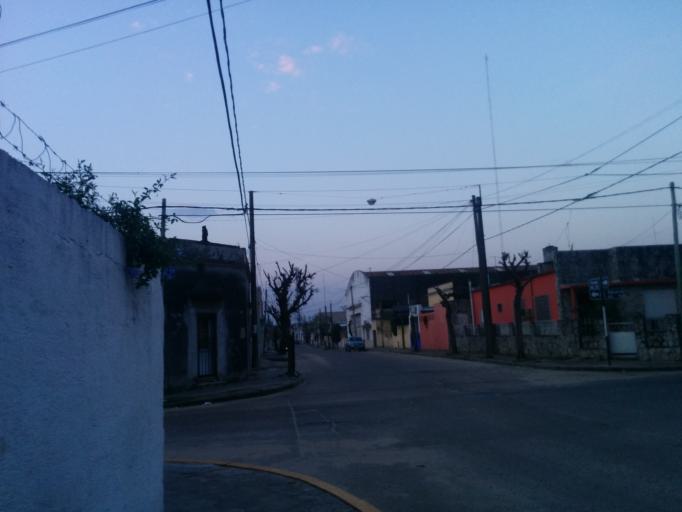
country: AR
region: Entre Rios
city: Concordia
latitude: -31.3865
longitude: -58.0207
